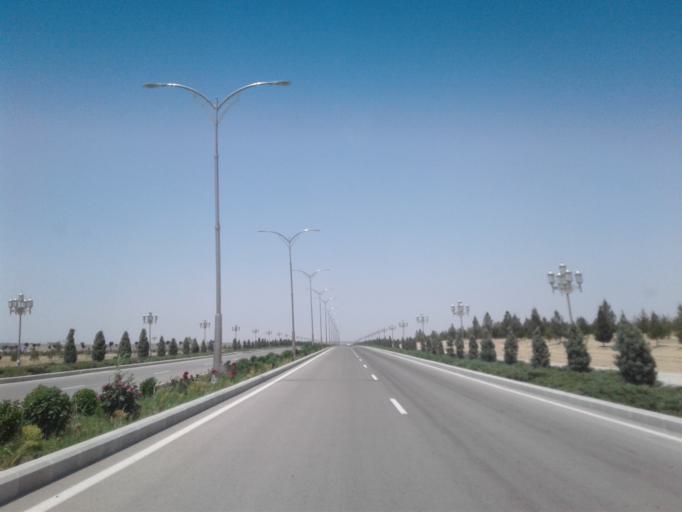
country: TM
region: Balkan
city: Turkmenbasy
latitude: 39.9823
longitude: 52.8359
